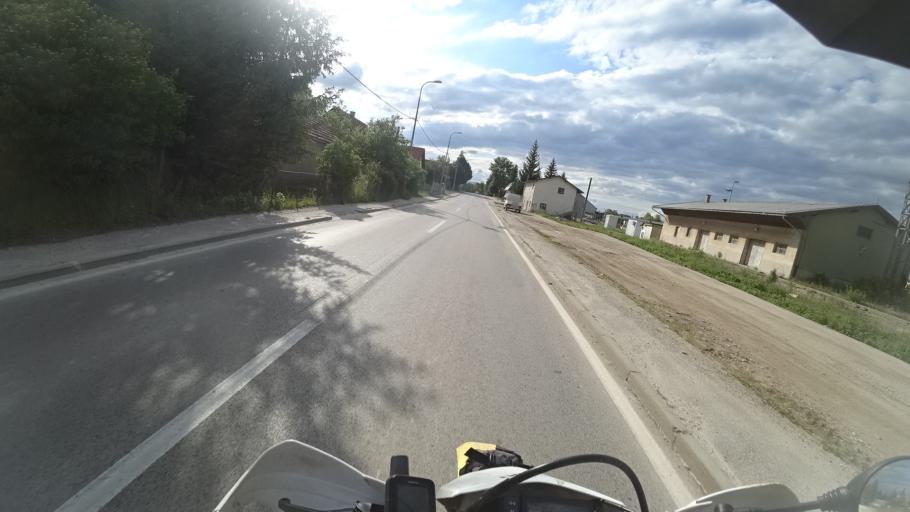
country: HR
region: Licko-Senjska
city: Gospic
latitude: 44.5349
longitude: 15.3950
